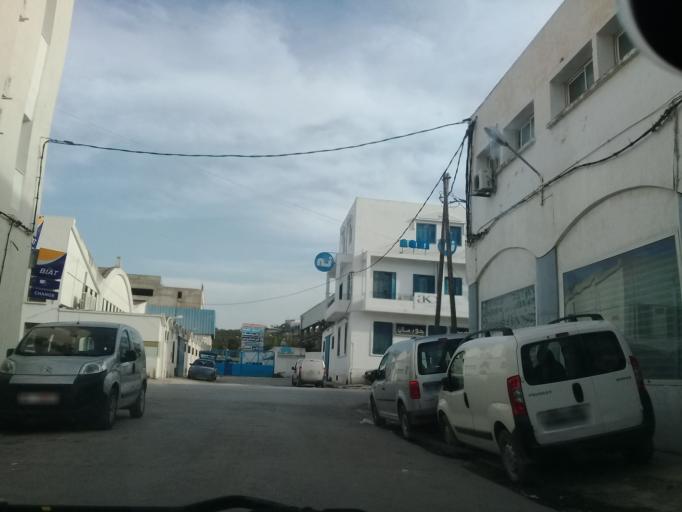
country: TN
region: Tunis
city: Tunis
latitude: 36.7904
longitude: 10.1848
